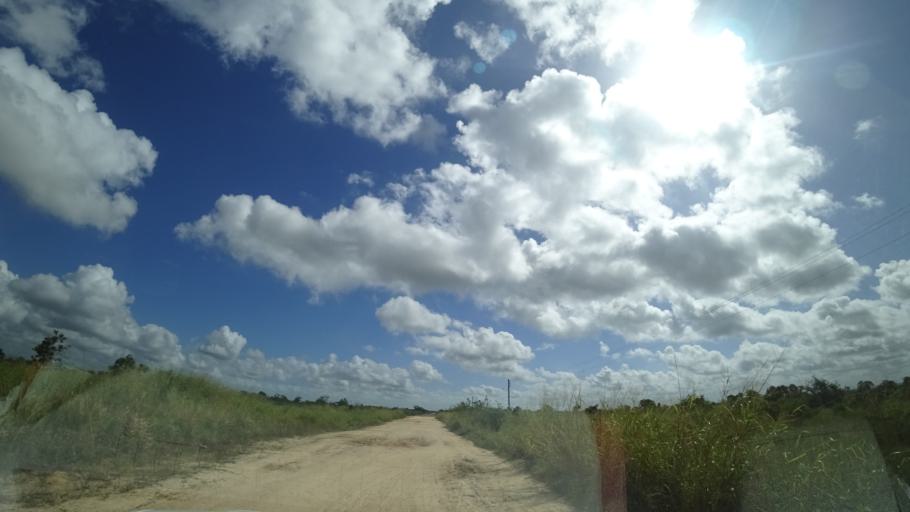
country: MZ
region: Sofala
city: Dondo
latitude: -19.4472
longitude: 34.5622
